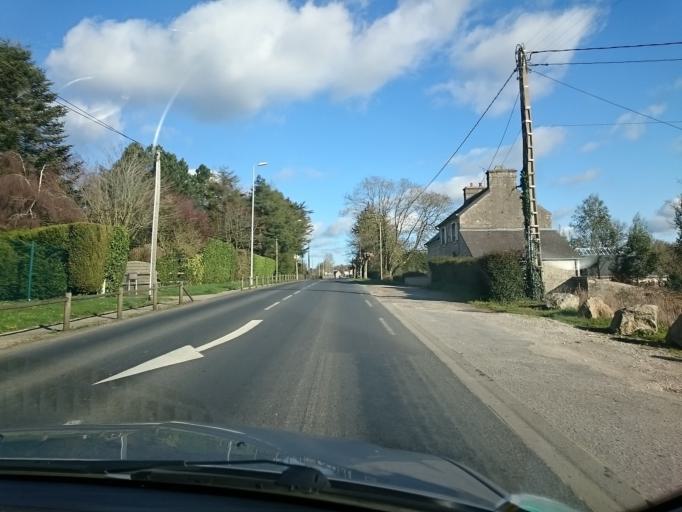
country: FR
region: Lower Normandy
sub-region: Departement de la Manche
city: Valognes
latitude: 49.5027
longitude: -1.4598
